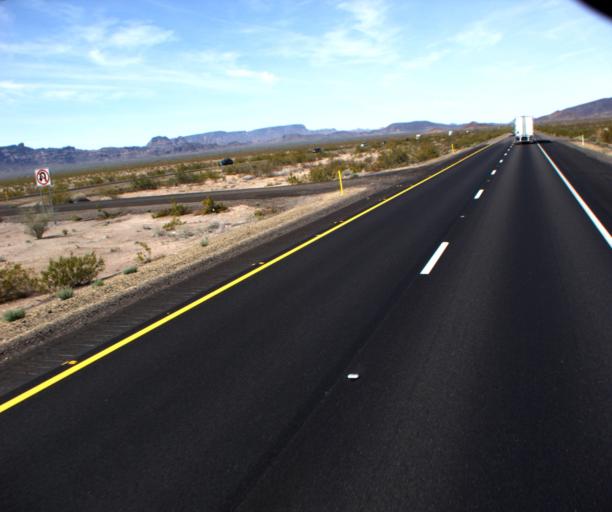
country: US
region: Arizona
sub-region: La Paz County
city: Salome
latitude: 33.6396
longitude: -113.8245
